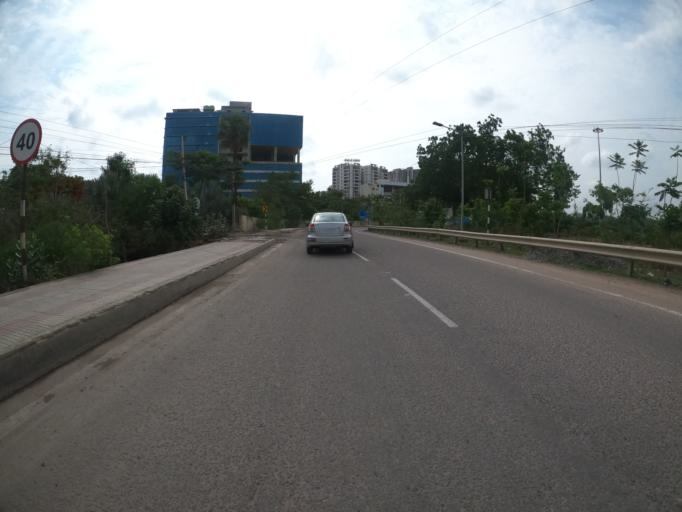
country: IN
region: Telangana
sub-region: Rangareddi
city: Kukatpalli
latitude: 17.4185
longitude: 78.3552
